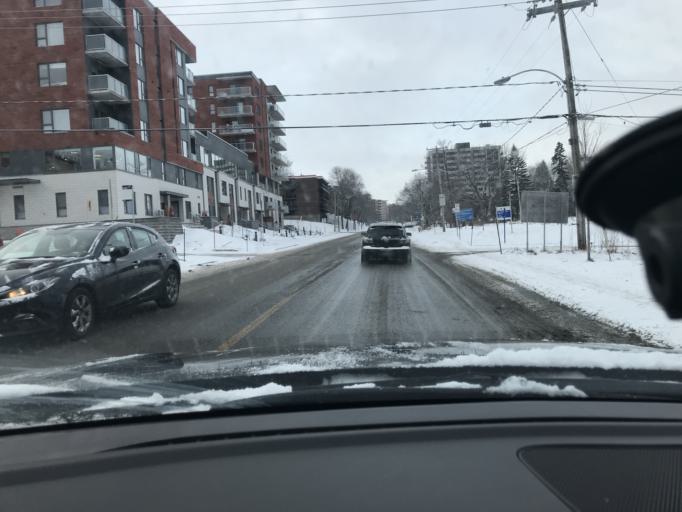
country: CA
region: Quebec
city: Quebec
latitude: 46.7911
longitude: -71.2735
